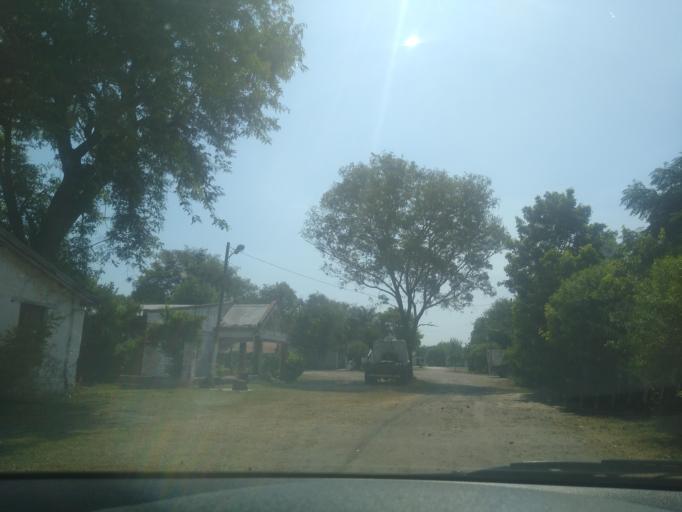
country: AR
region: Chaco
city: Puerto Tirol
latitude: -27.5609
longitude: -59.3051
